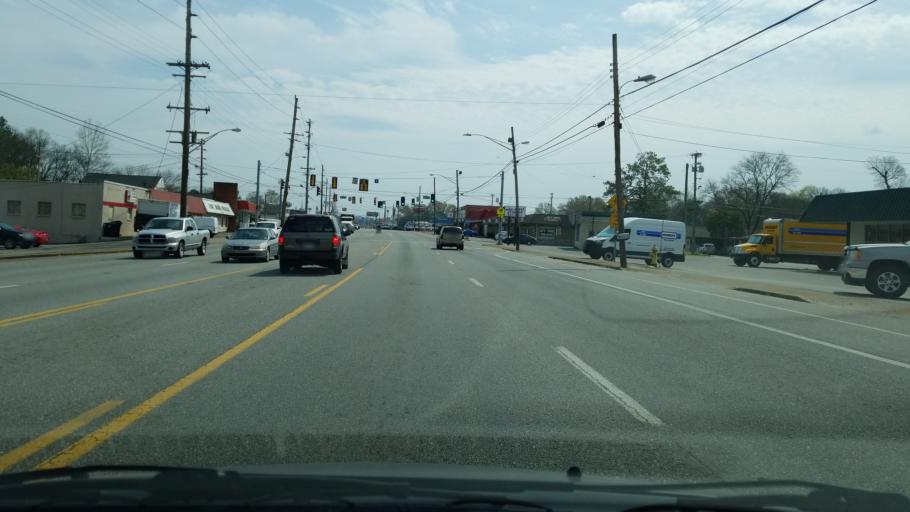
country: US
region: Tennessee
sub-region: Hamilton County
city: East Ridge
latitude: 34.9907
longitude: -85.2218
